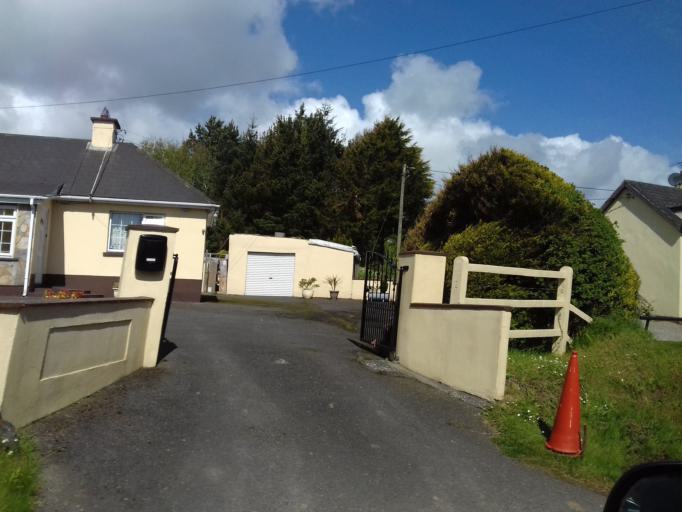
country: IE
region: Leinster
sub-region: Loch Garman
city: Castlebridge
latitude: 52.3730
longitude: -6.4334
